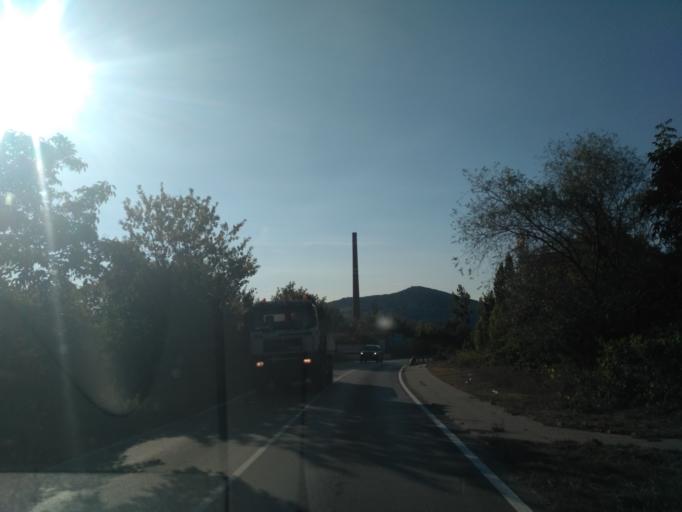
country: SK
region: Kosicky
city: Kosice
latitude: 48.7473
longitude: 21.2682
